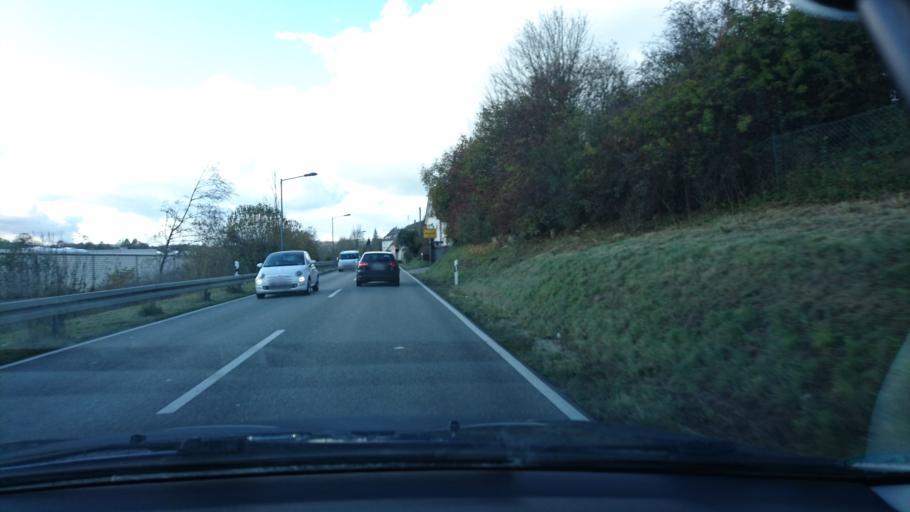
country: DE
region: Baden-Wuerttemberg
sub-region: Regierungsbezirk Stuttgart
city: Abtsgmund
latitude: 48.8953
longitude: 10.0252
